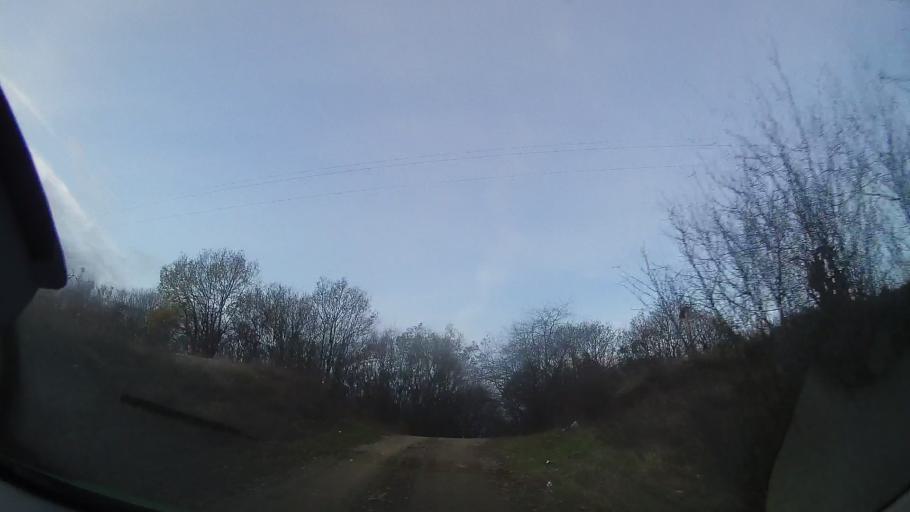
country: RO
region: Cluj
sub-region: Comuna Palatca
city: Palatca
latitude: 46.8597
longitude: 24.0262
